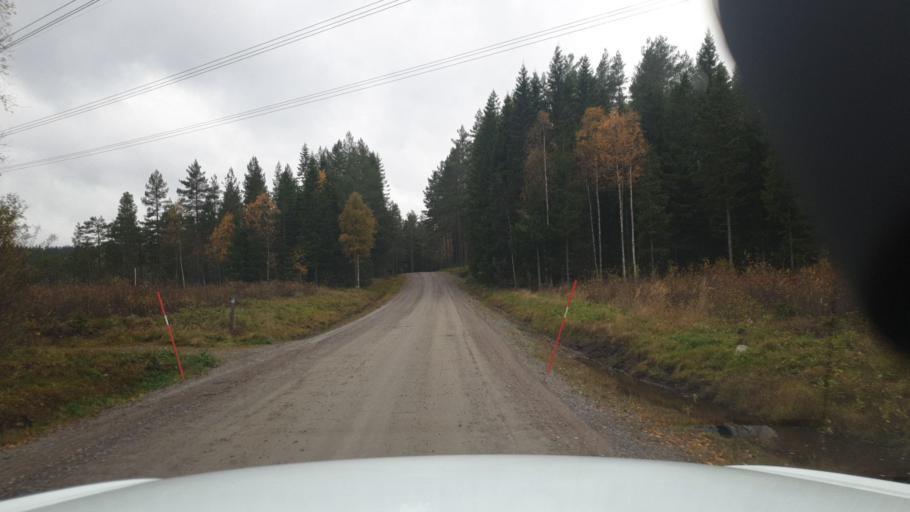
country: SE
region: Vaermland
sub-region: Sunne Kommun
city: Sunne
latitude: 59.8345
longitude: 12.9234
